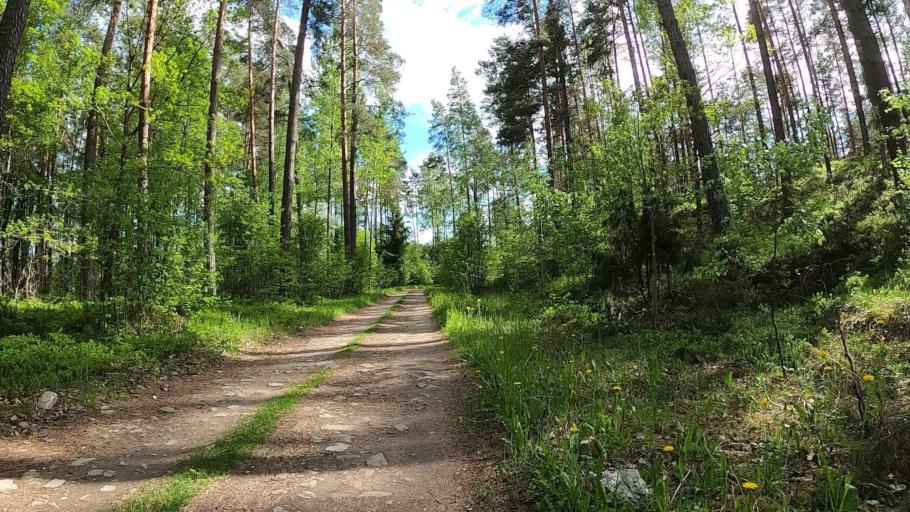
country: LV
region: Jurmala
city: Jurmala
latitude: 56.9018
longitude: 23.8259
